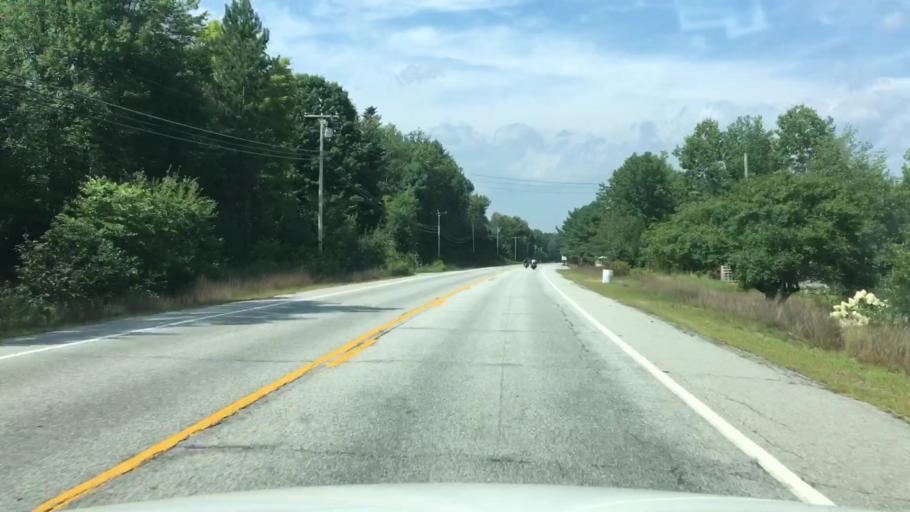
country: US
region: Maine
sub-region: Oxford County
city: Peru
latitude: 44.4968
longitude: -70.3922
